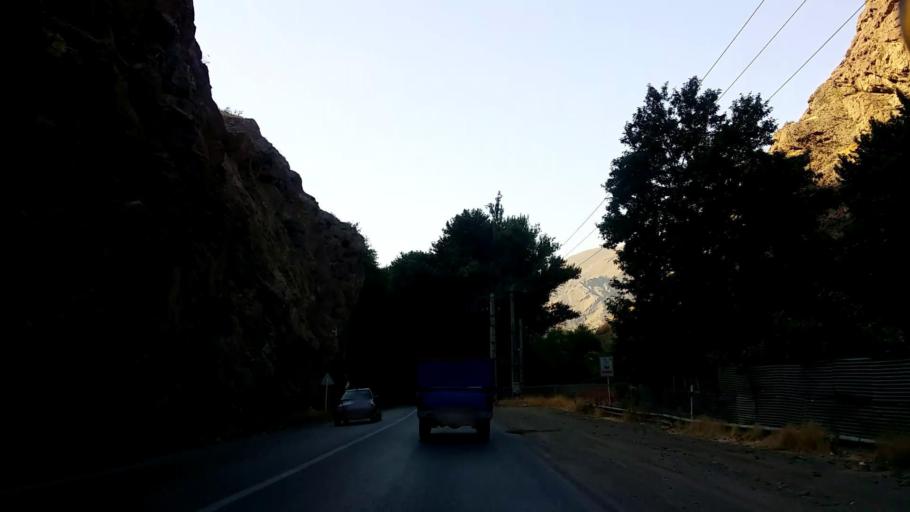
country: IR
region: Alborz
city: Karaj
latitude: 35.8956
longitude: 51.0454
